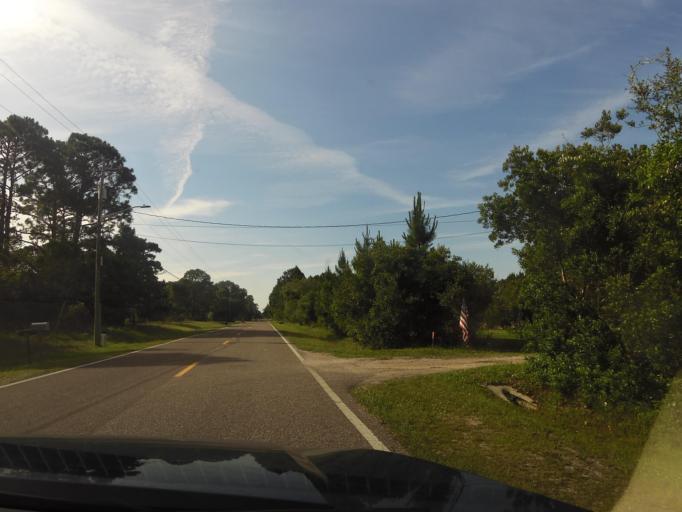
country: US
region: Florida
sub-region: Nassau County
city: Fernandina Beach
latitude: 30.5181
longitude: -81.4794
